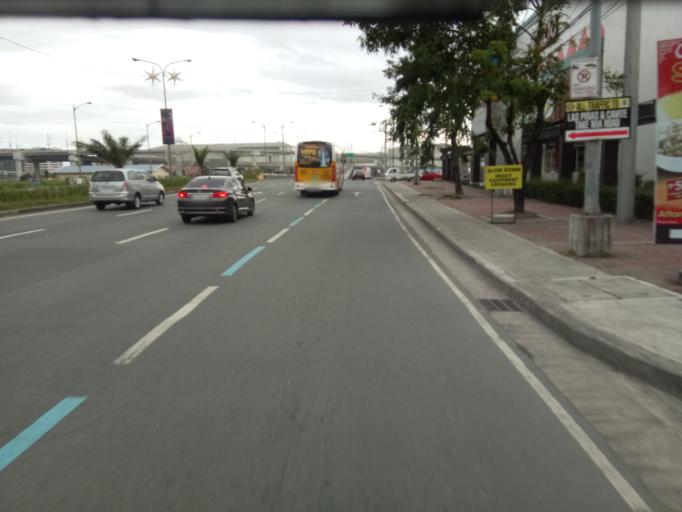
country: PH
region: Metro Manila
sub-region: Makati City
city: Makati City
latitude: 14.5207
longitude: 120.9907
